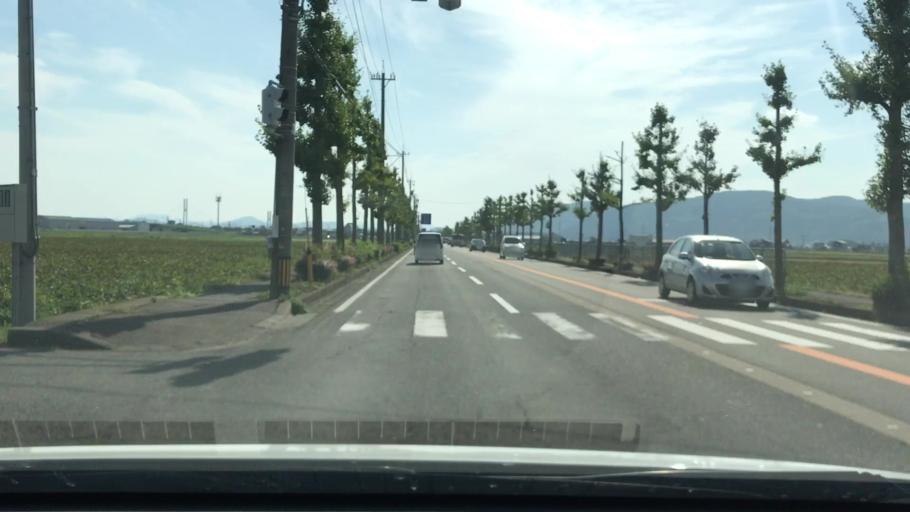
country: JP
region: Fukui
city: Fukui-shi
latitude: 36.1119
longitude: 136.2164
